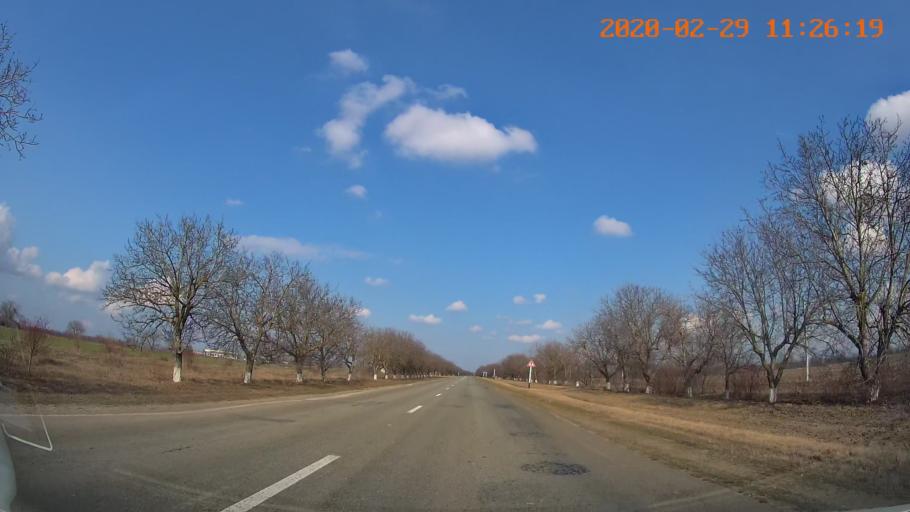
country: MD
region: Telenesti
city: Cocieri
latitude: 47.4516
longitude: 29.1465
